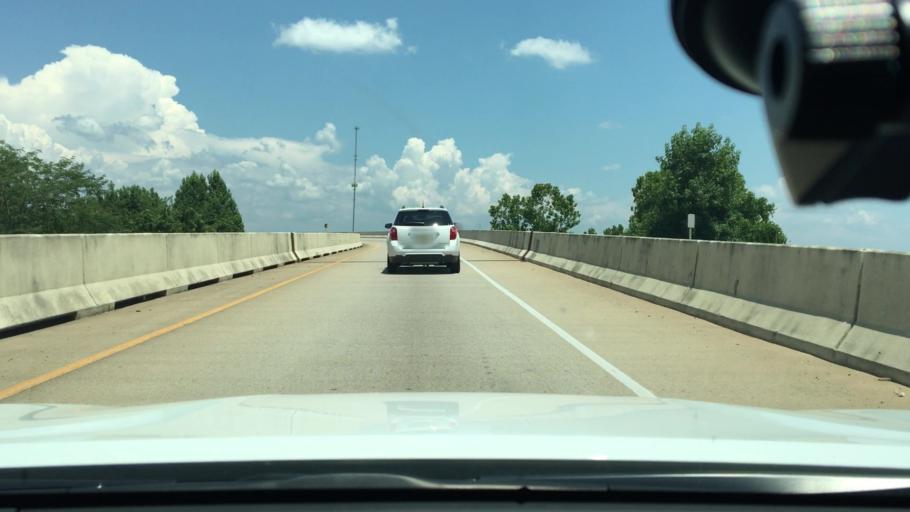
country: US
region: Arkansas
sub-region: Crawford County
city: Alma
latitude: 35.4806
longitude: -94.2441
